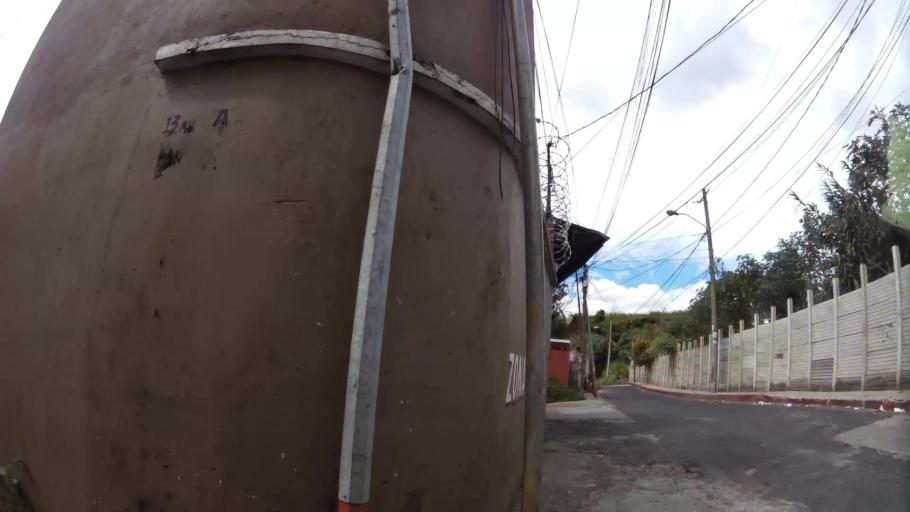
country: GT
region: Guatemala
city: Santa Catarina Pinula
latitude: 14.5694
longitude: -90.5302
